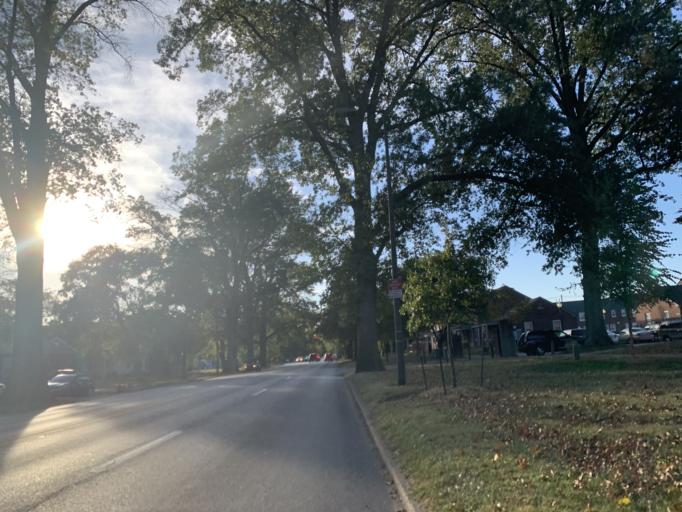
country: US
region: Kentucky
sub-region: Jefferson County
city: Shively
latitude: 38.2231
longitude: -85.7908
